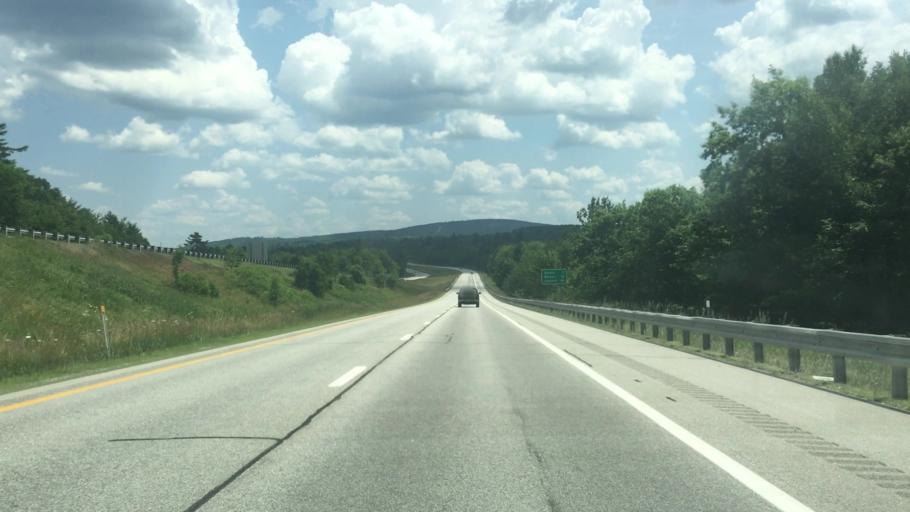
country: US
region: New Hampshire
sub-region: Merrimack County
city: New London
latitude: 43.4123
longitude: -72.0289
